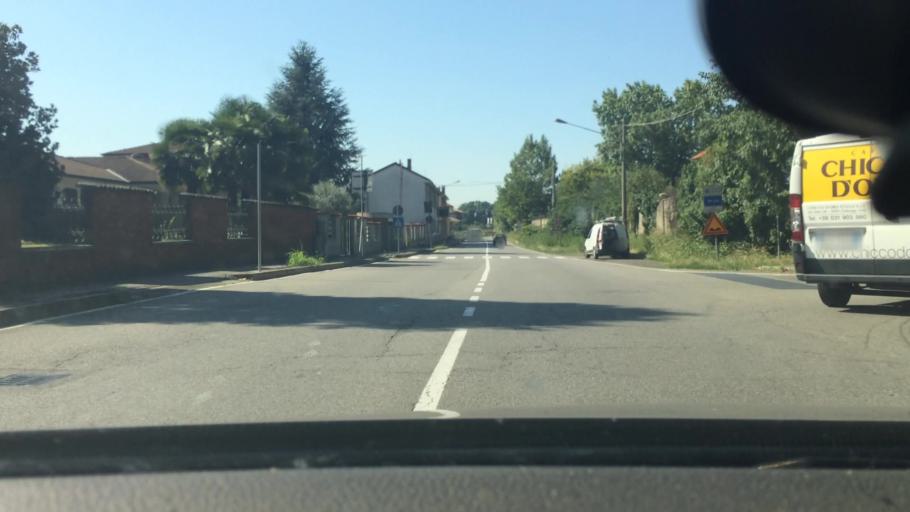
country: IT
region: Lombardy
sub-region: Citta metropolitana di Milano
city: Casorezzo
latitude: 45.5223
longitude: 8.9058
